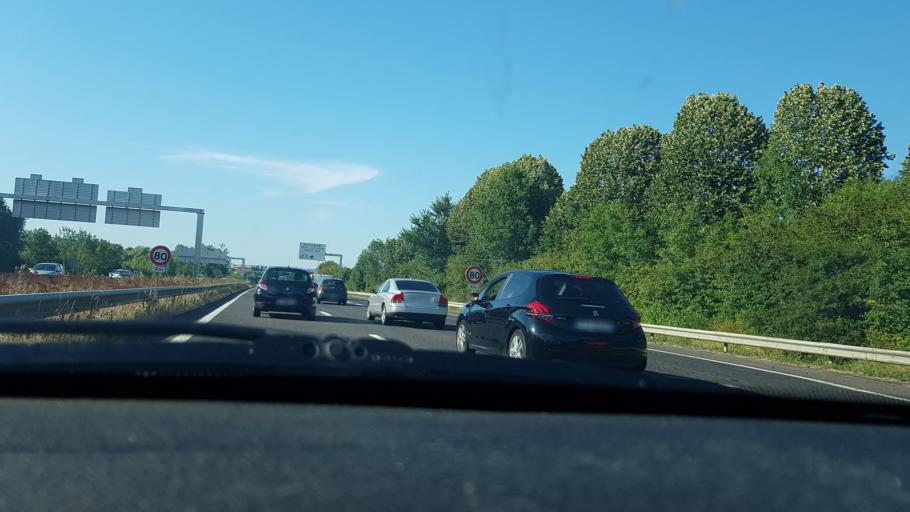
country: FR
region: Lorraine
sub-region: Departement de Meurthe-et-Moselle
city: Vandoeuvre-les-Nancy
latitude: 48.6314
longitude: 6.1824
